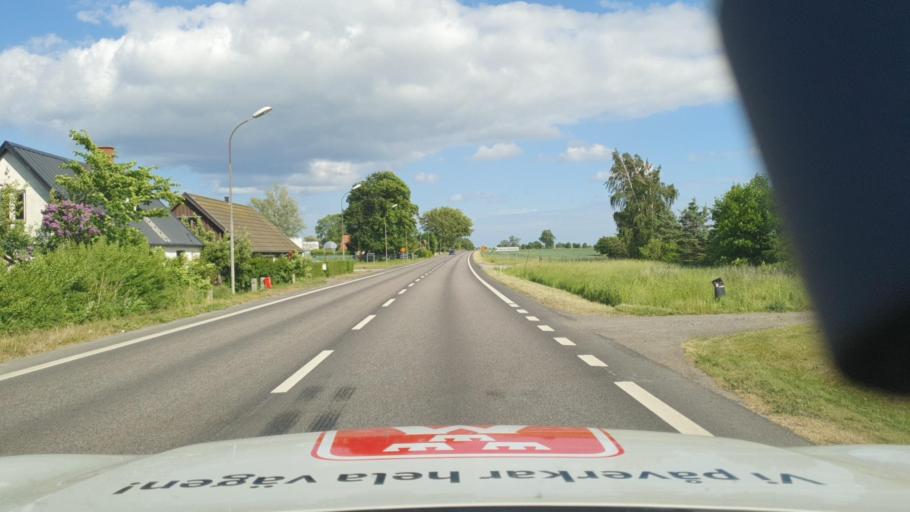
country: SE
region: Skane
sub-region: Simrishamns Kommun
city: Kivik
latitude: 55.5442
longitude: 14.1919
